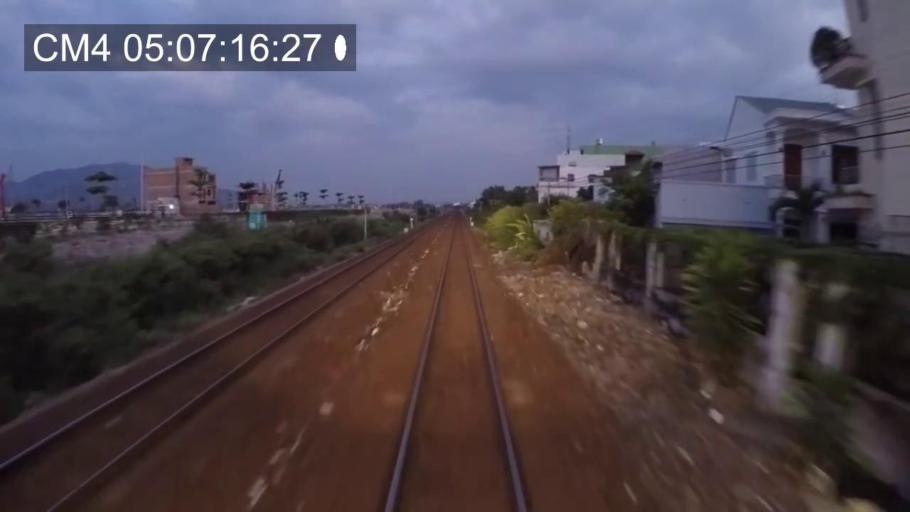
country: VN
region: Khanh Hoa
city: Nha Trang
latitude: 12.2838
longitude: 109.1835
